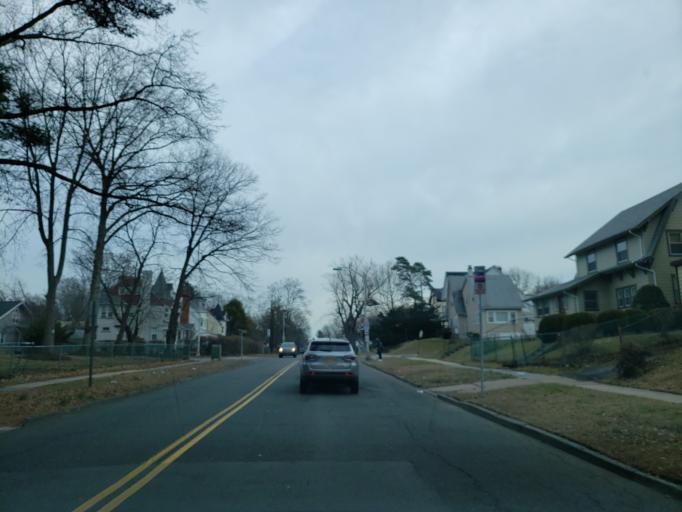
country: US
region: New Jersey
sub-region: Essex County
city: Orange
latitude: 40.7781
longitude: -74.2178
